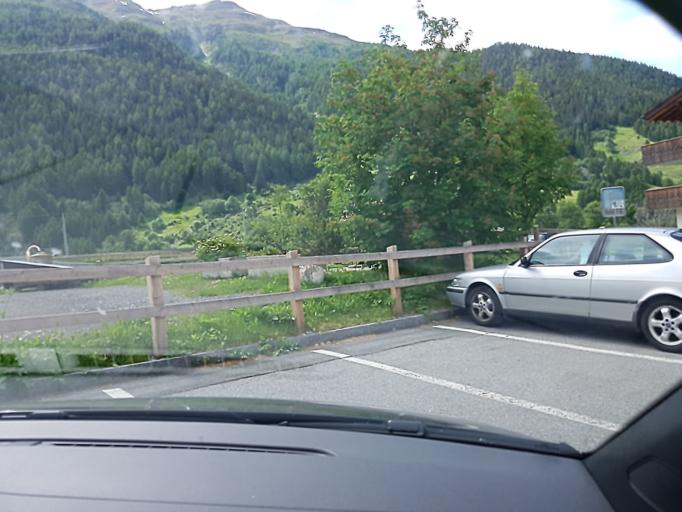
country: CH
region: Grisons
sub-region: Inn District
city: Zernez
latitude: 46.6998
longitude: 10.0919
